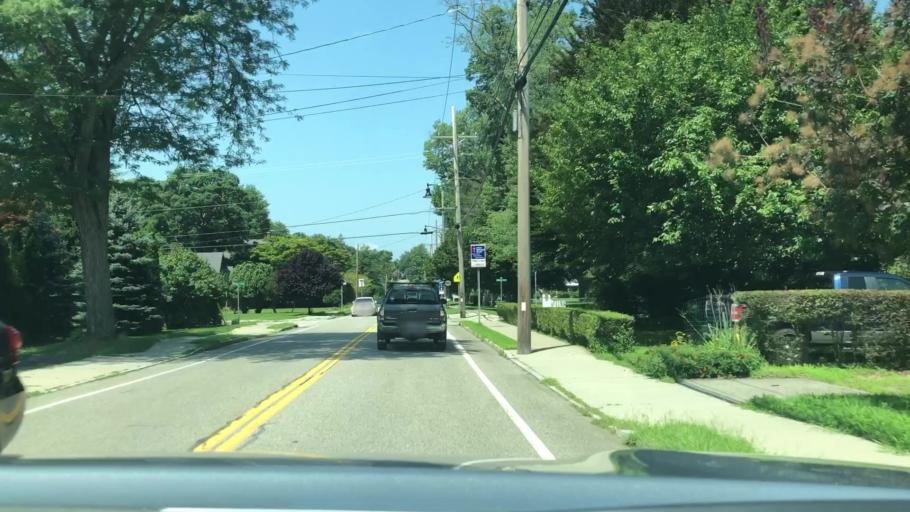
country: US
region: New York
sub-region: Dutchess County
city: Beacon
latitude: 41.4963
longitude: -73.9628
